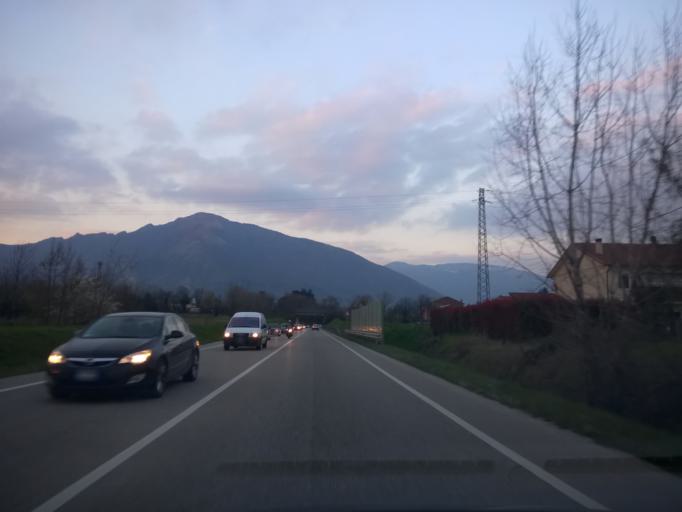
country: IT
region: Veneto
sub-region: Provincia di Vicenza
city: Schio
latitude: 45.7064
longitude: 11.3765
